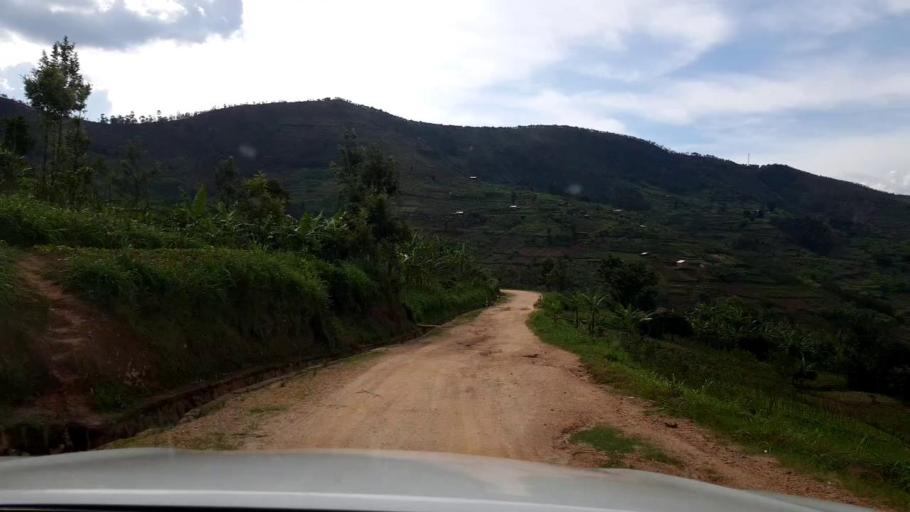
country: RW
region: Southern Province
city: Gitarama
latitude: -1.9782
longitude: 29.7106
